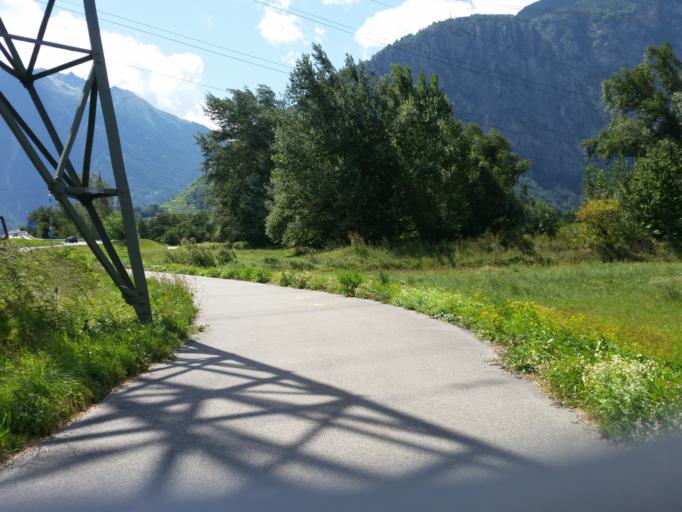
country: CH
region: Valais
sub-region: Martigny District
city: Martigny-Ville
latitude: 46.1173
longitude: 7.0801
